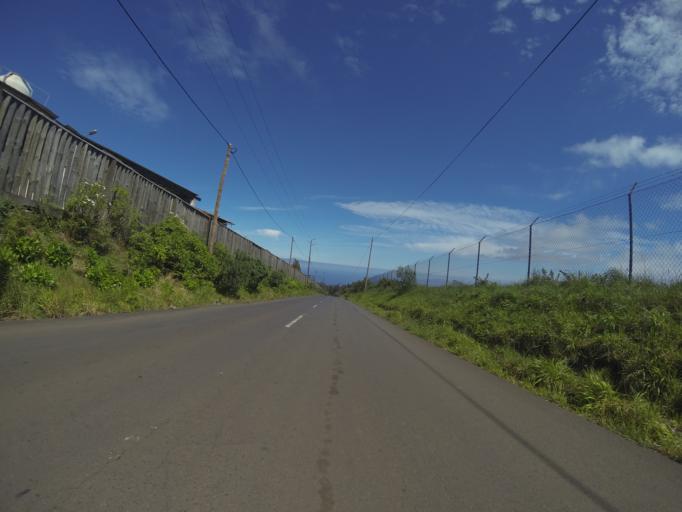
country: PT
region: Madeira
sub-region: Santa Cruz
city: Camacha
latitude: 32.7163
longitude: -16.8308
